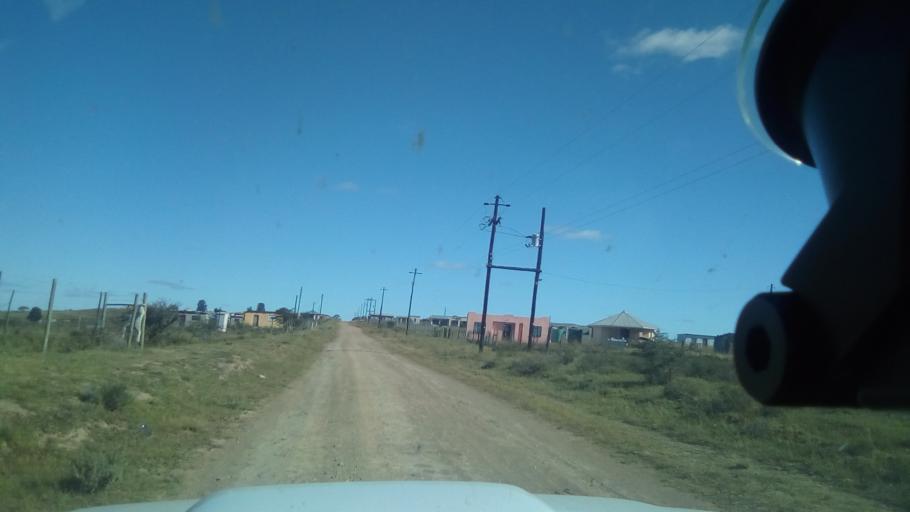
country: ZA
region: Eastern Cape
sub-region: Buffalo City Metropolitan Municipality
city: Bhisho
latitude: -32.7850
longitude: 27.3307
